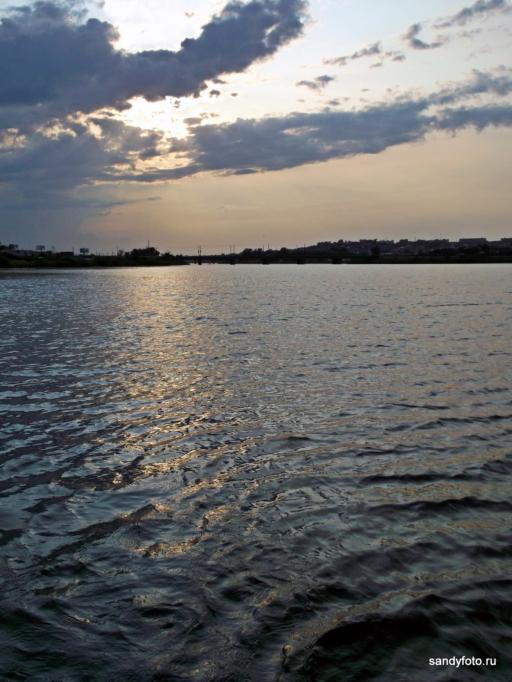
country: RU
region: Chelyabinsk
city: Troitsk
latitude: 54.0885
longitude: 61.5846
